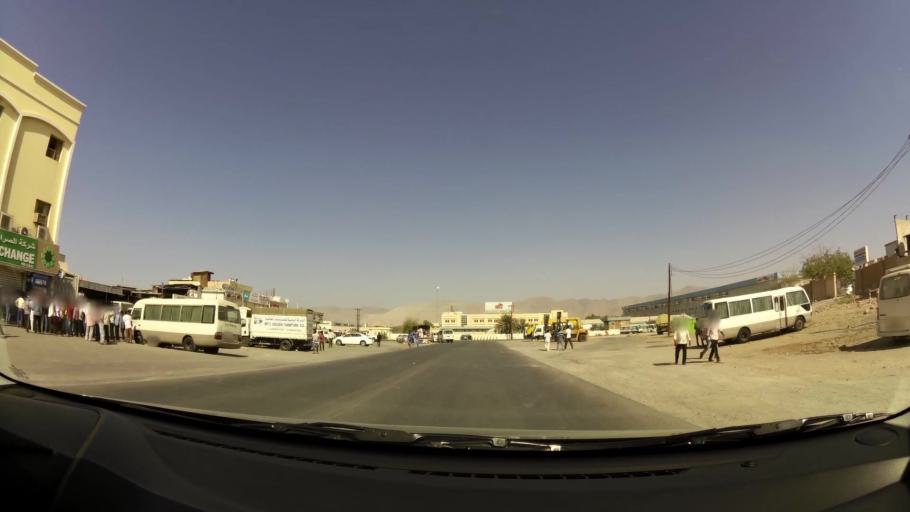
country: OM
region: Muhafazat Masqat
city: Bawshar
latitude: 23.5760
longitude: 58.3521
